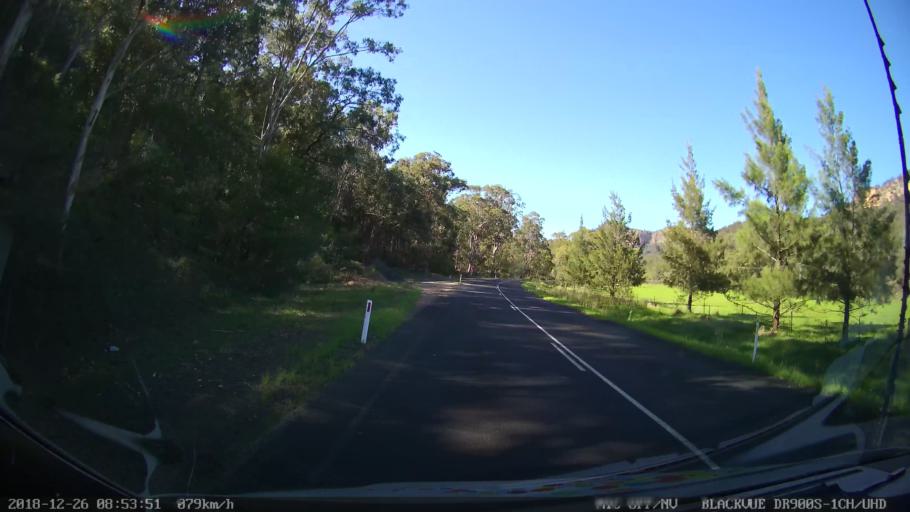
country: AU
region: New South Wales
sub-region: Mid-Western Regional
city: Kandos
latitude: -32.6087
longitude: 150.0757
